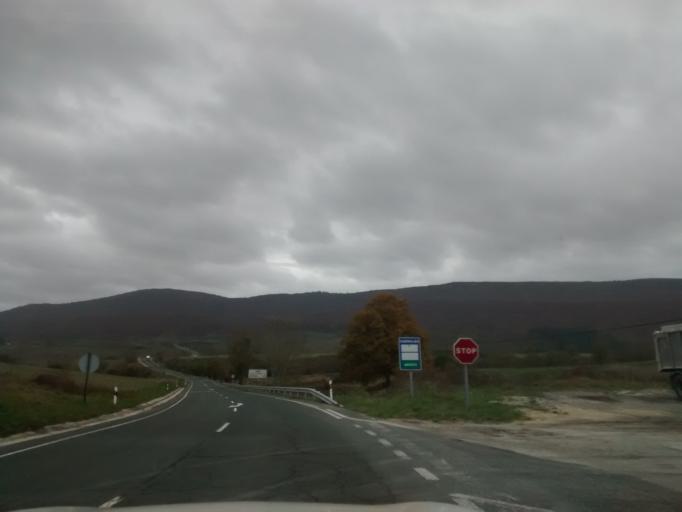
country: ES
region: Castille and Leon
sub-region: Provincia de Burgos
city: Arija
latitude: 42.9704
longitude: -3.8494
